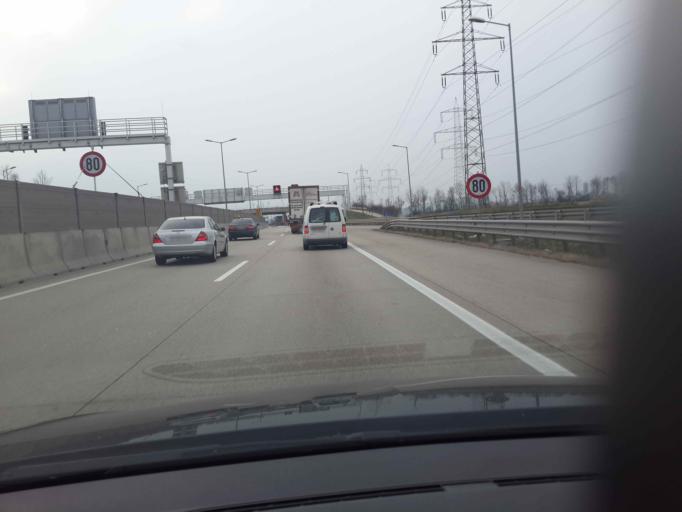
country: AT
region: Lower Austria
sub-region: Politischer Bezirk Wien-Umgebung
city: Leopoldsdorf
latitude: 48.1274
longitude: 16.3854
